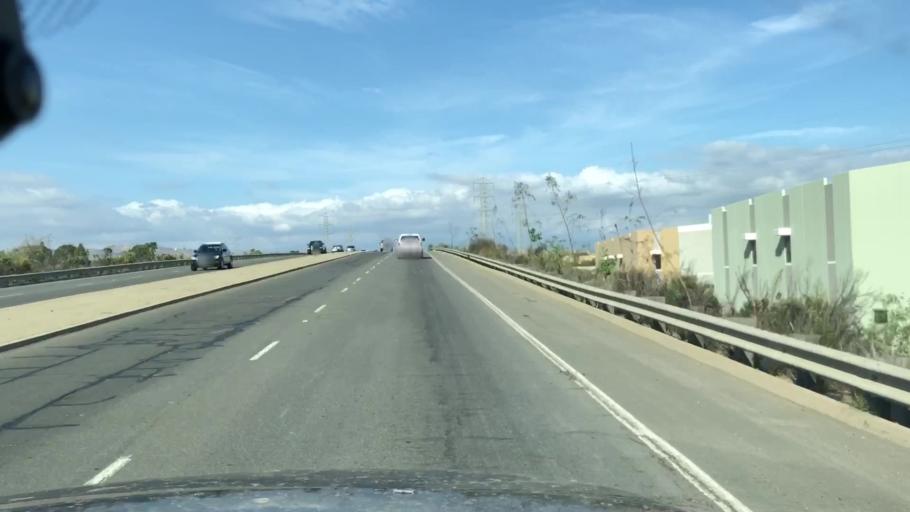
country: US
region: California
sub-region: Ventura County
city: El Rio
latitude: 34.2462
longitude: -119.2140
